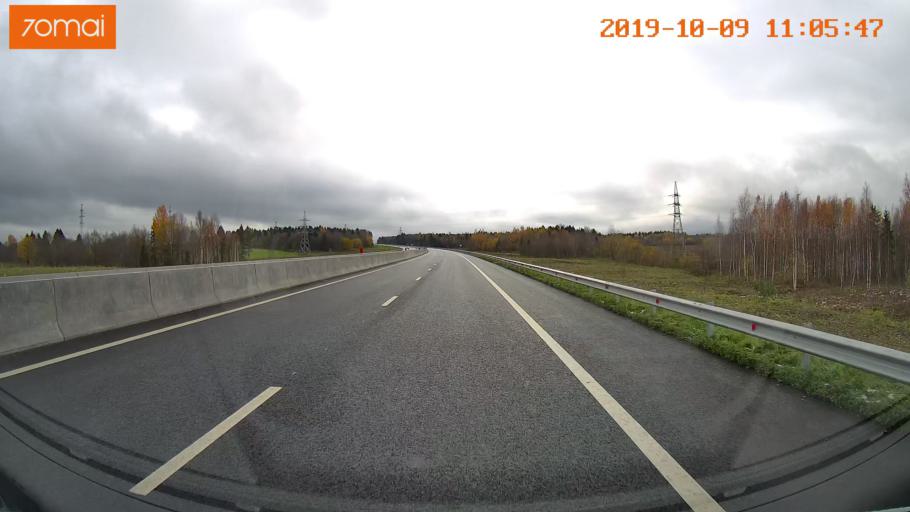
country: RU
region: Vologda
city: Molochnoye
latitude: 59.1950
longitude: 39.7580
